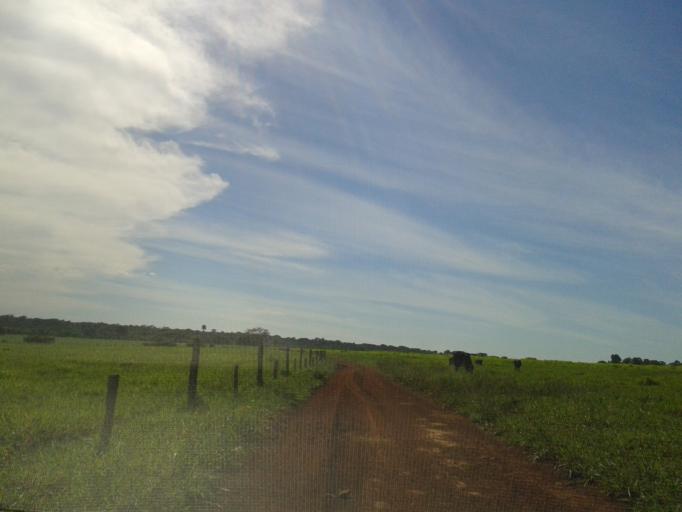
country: BR
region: Minas Gerais
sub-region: Capinopolis
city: Capinopolis
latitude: -18.6249
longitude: -49.7403
